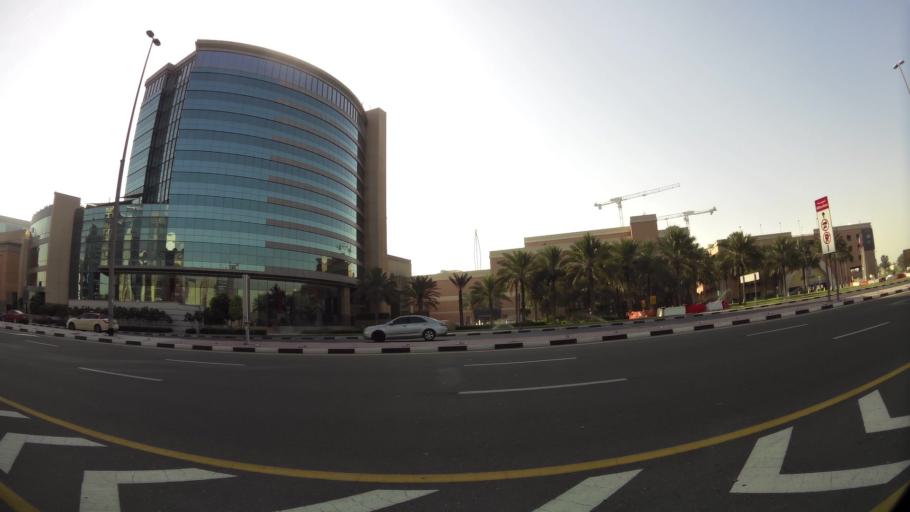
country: AE
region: Ash Shariqah
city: Sharjah
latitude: 25.2528
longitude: 55.3297
